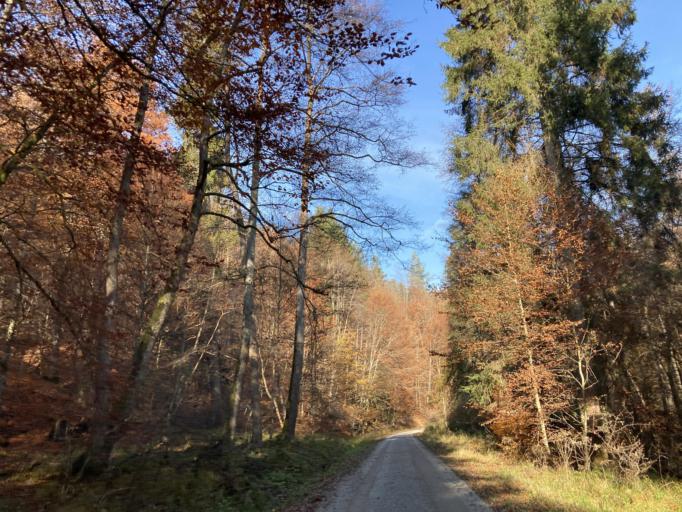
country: DE
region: Baden-Wuerttemberg
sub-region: Regierungsbezirk Stuttgart
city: Weil im Schonbuch
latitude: 48.5835
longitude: 9.0380
